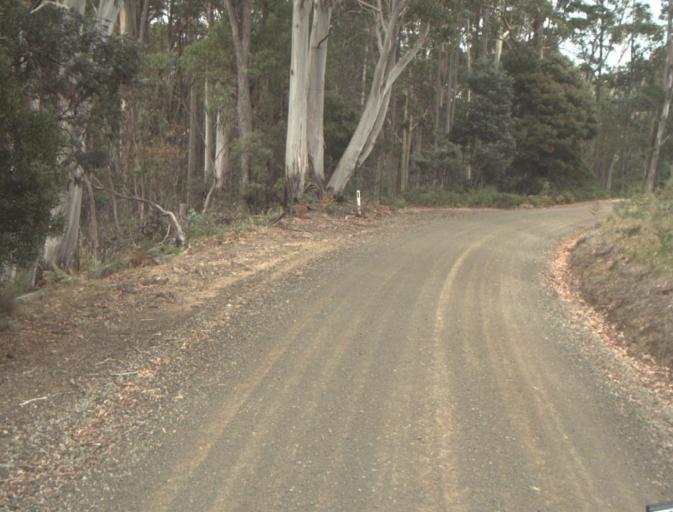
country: AU
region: Tasmania
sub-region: Northern Midlands
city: Evandale
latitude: -41.4540
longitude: 147.4762
